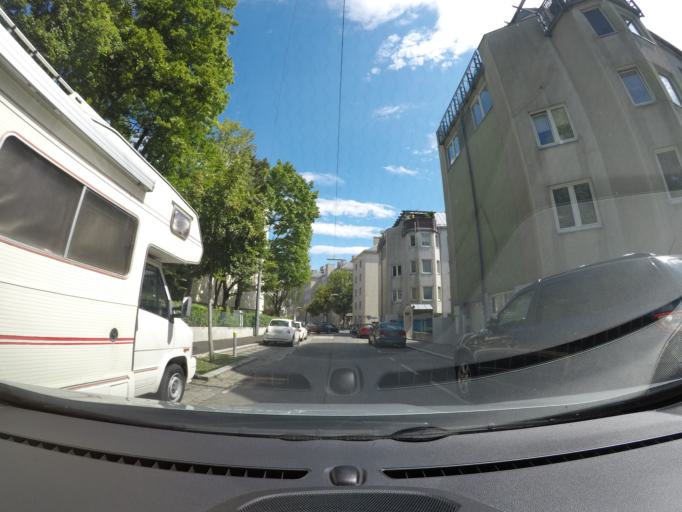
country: AT
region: Lower Austria
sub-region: Politischer Bezirk Modling
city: Perchtoldsdorf
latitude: 48.1942
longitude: 16.2668
